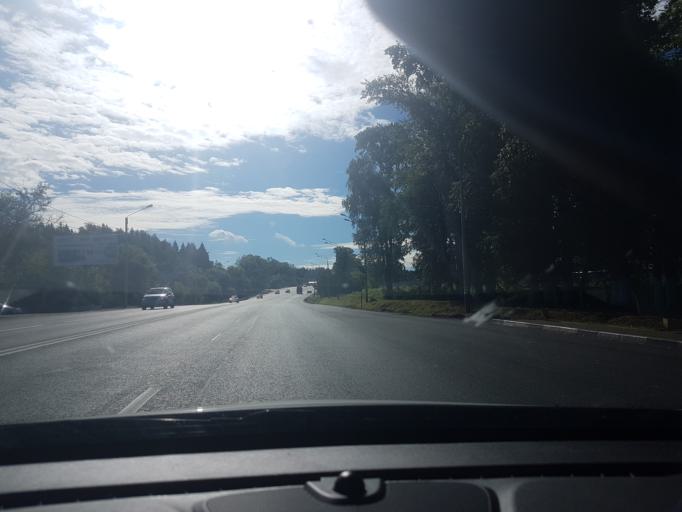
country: RU
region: Moskovskaya
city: Istra
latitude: 55.9052
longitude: 36.8908
